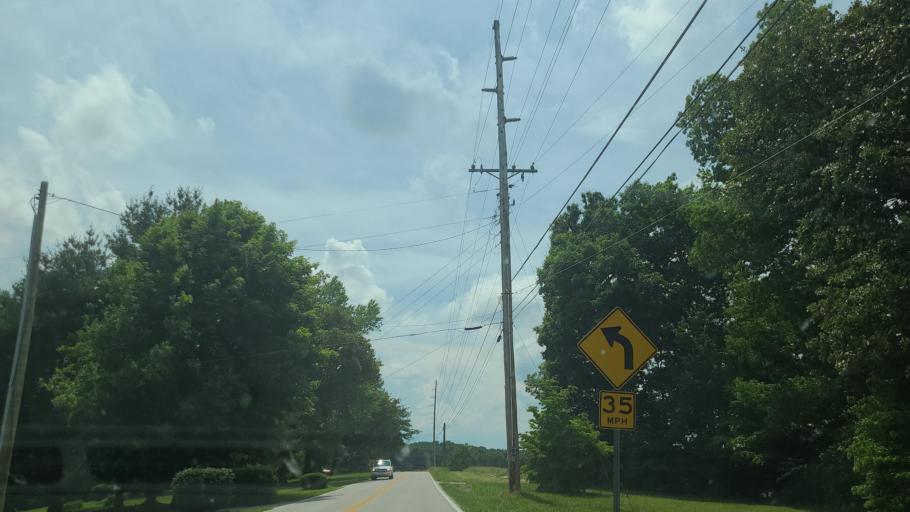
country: US
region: Tennessee
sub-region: Cumberland County
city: Crossville
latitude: 35.9095
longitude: -85.0229
